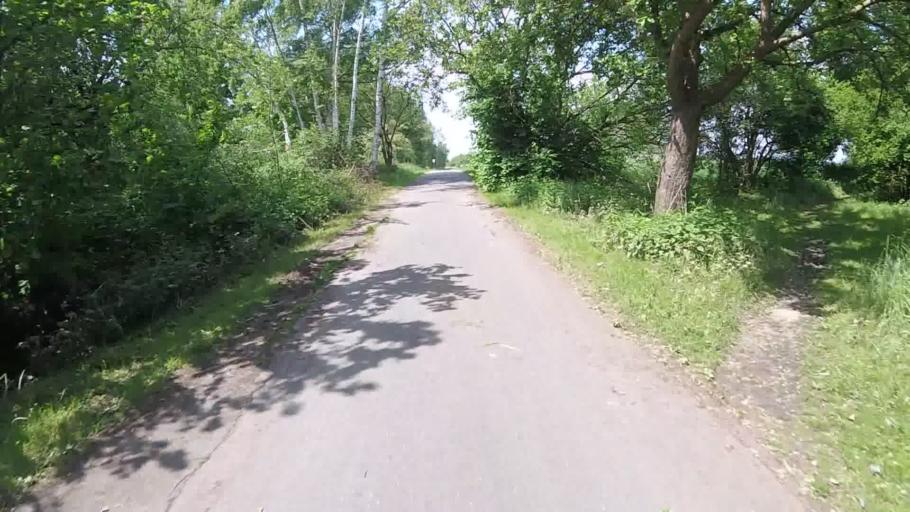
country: DE
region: Hamburg
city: Bergedorf
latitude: 53.4892
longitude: 10.1729
